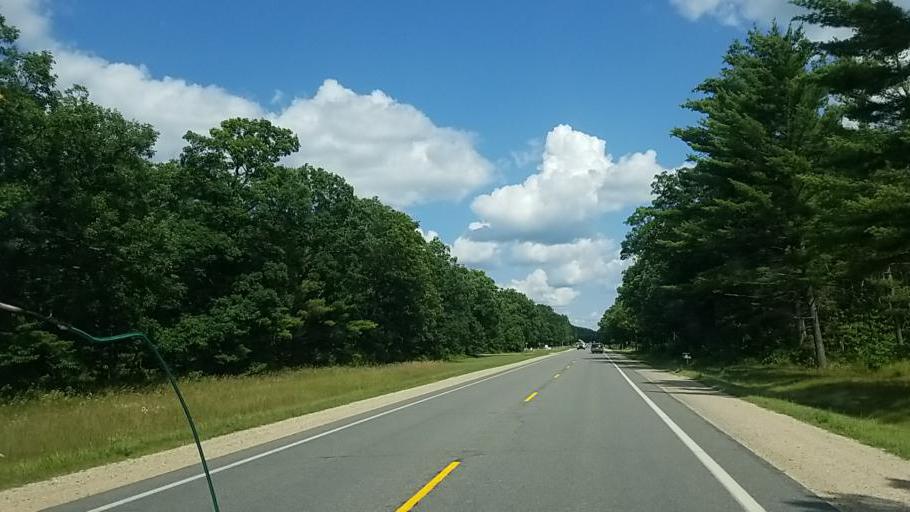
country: US
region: Michigan
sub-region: Newaygo County
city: Newaygo
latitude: 43.4059
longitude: -85.6993
